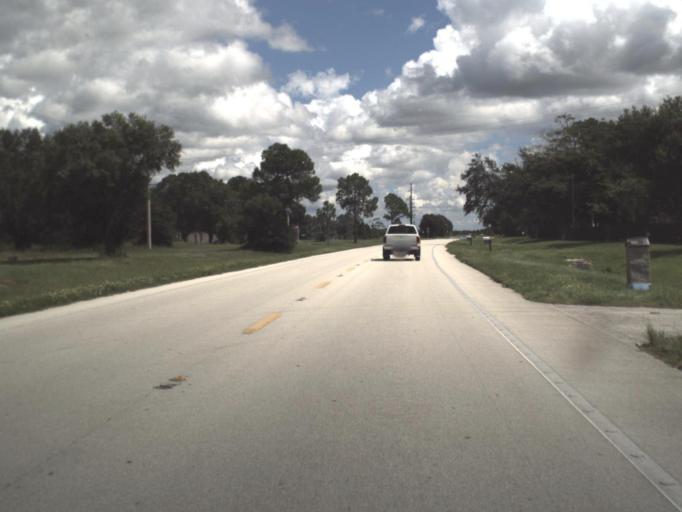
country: US
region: Florida
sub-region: DeSoto County
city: Southeast Arcadia
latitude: 27.2091
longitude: -81.7994
